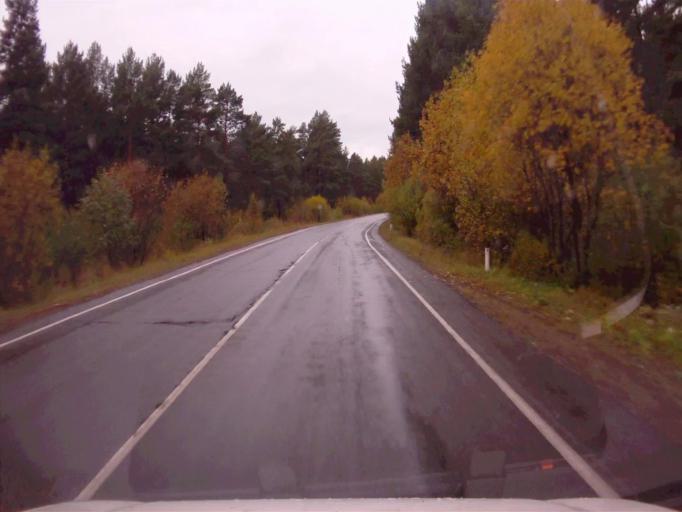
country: RU
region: Chelyabinsk
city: Verkhniy Ufaley
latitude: 56.0513
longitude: 60.1657
